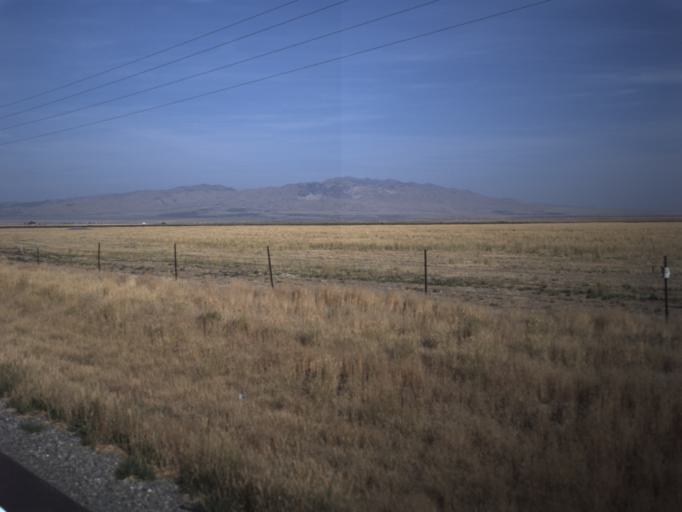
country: US
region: Idaho
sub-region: Oneida County
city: Malad City
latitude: 41.9672
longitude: -112.8479
